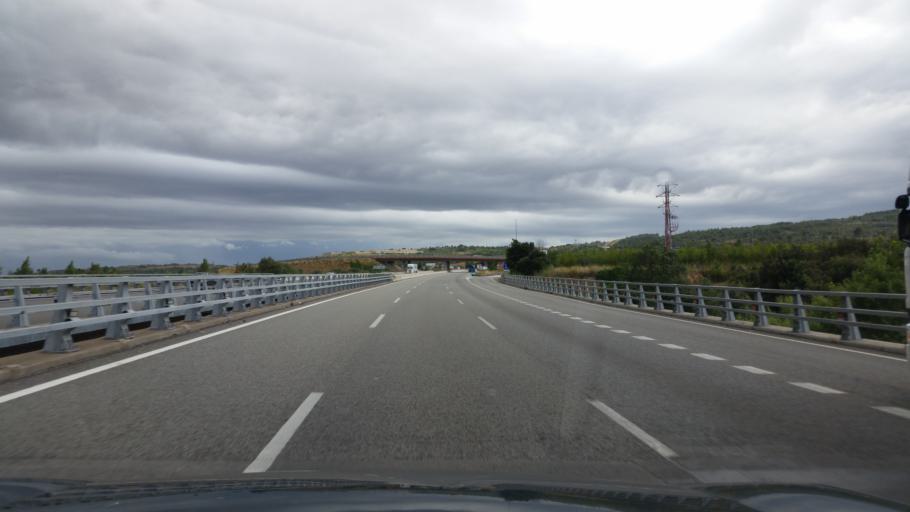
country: ES
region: Catalonia
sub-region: Provincia de Girona
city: Pont de Molins
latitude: 42.3028
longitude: 2.9448
